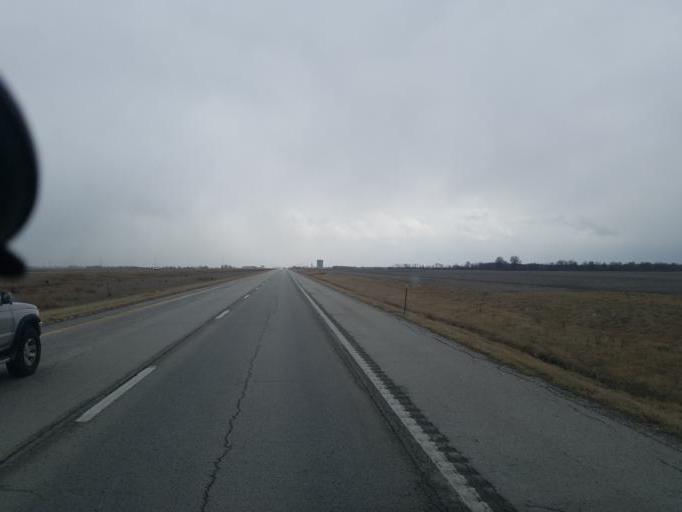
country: US
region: Missouri
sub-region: Randolph County
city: Moberly
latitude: 39.5624
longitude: -92.4605
